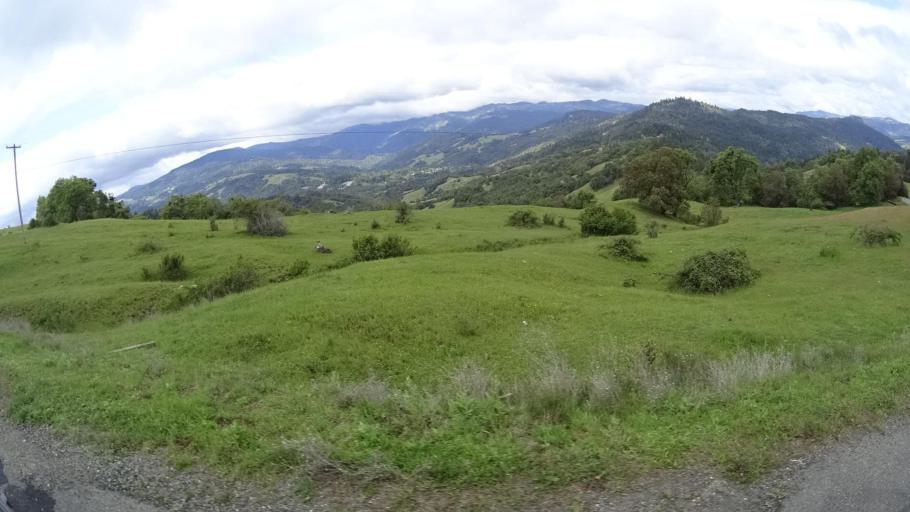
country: US
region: California
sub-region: Humboldt County
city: Redway
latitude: 40.1805
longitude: -123.5716
